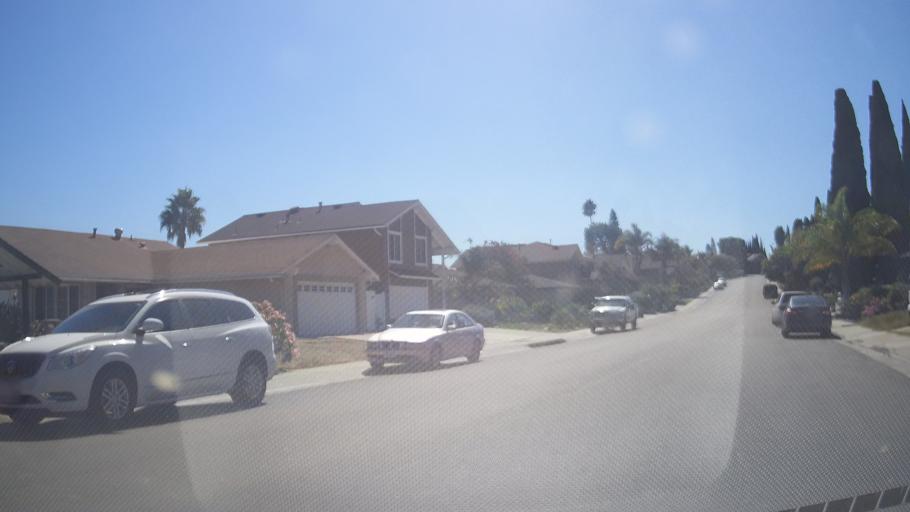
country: US
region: California
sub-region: San Diego County
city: Poway
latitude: 32.9899
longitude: -117.0853
